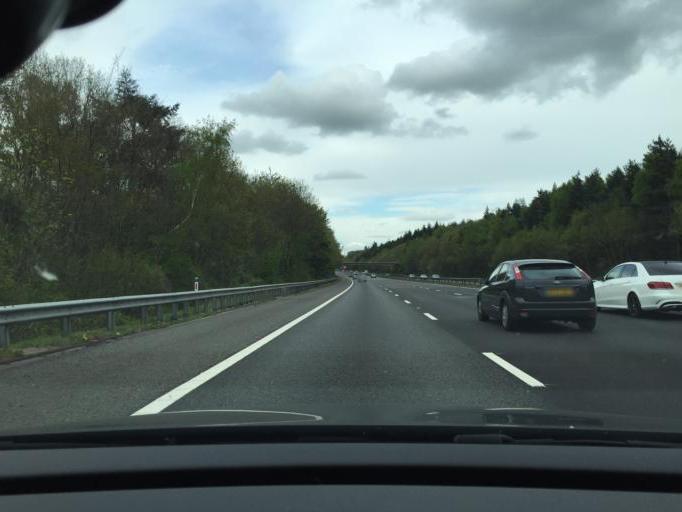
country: GB
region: England
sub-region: West Berkshire
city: Basildon
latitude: 51.4604
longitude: -1.1652
